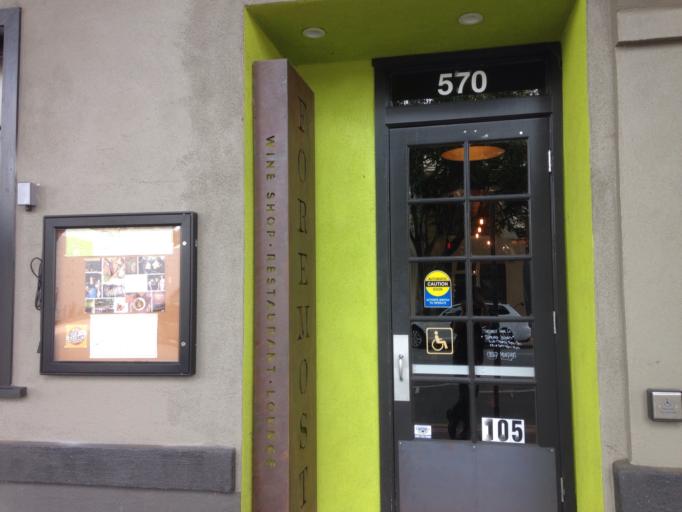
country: US
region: California
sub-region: San Luis Obispo County
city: San Luis Obispo
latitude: 35.2778
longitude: -120.6664
